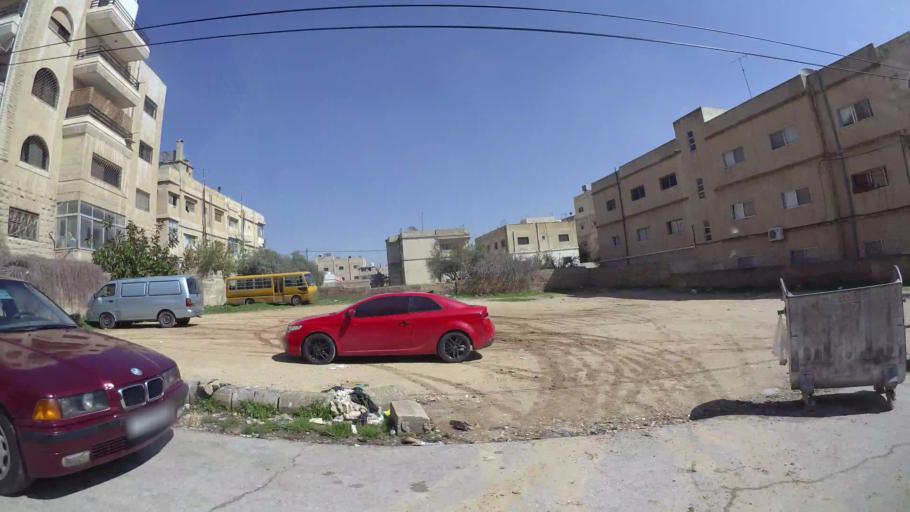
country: JO
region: Amman
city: Amman
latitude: 31.9767
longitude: 35.9861
